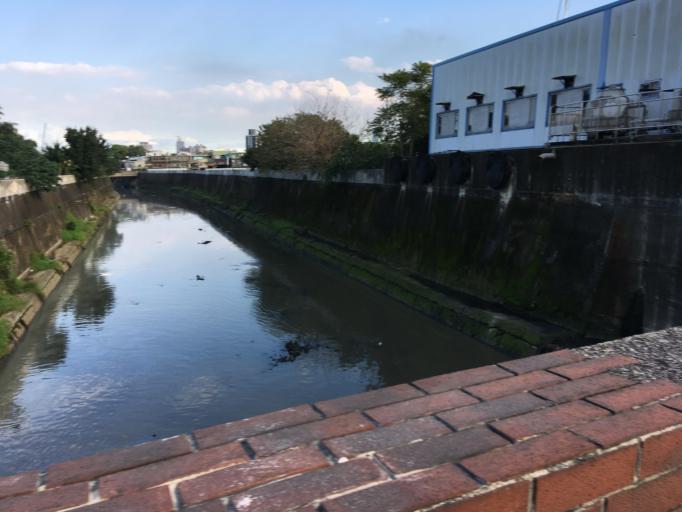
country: TW
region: Taipei
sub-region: Taipei
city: Banqiao
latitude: 25.0279
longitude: 121.4350
